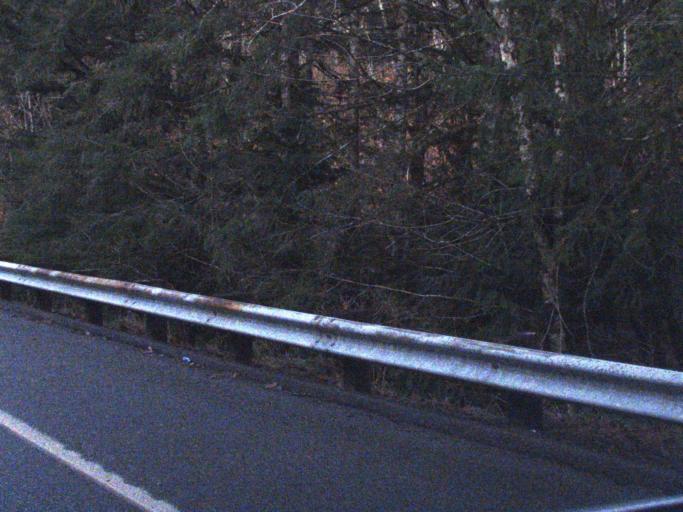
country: US
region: Washington
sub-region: Snohomish County
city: Darrington
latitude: 48.4988
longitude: -121.6465
